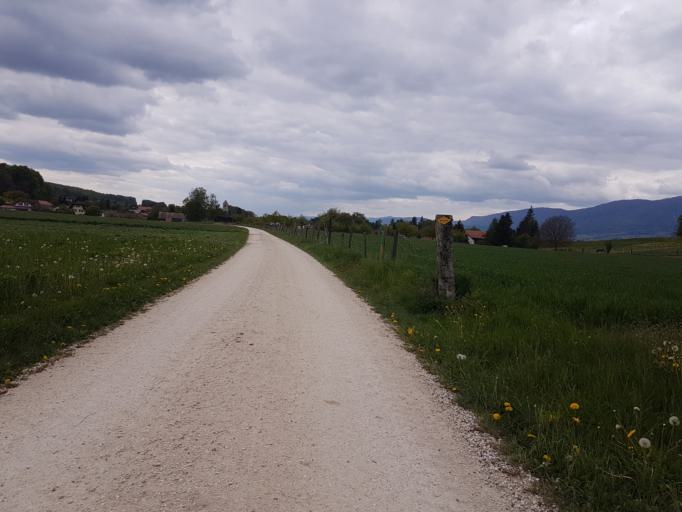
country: CH
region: Solothurn
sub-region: Bezirk Lebern
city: Langendorf
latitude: 47.1903
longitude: 7.5082
